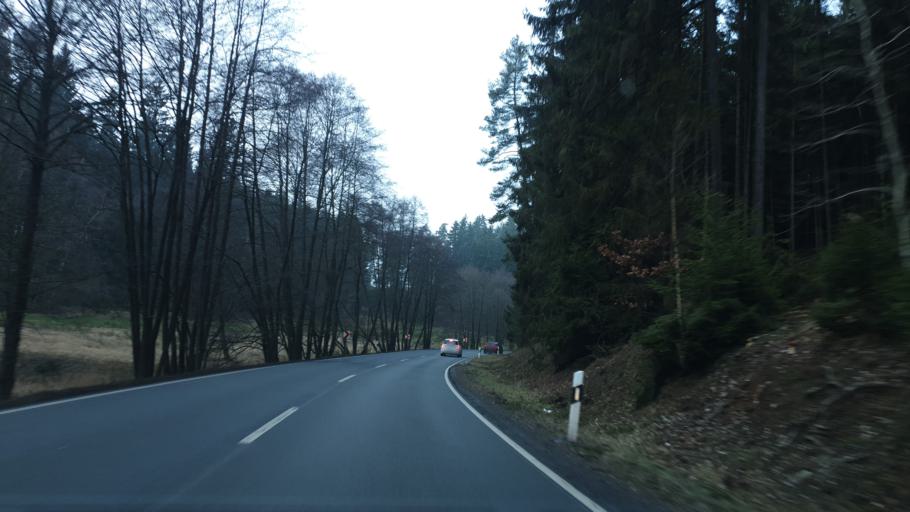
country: DE
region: Saxony
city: Bad Brambach
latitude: 50.2507
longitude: 12.3026
